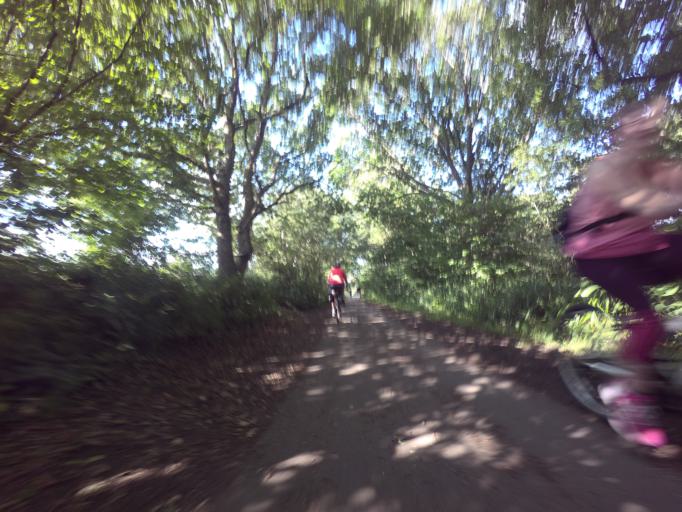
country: GB
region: England
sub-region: East Sussex
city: Hailsham
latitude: 50.8942
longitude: 0.2549
